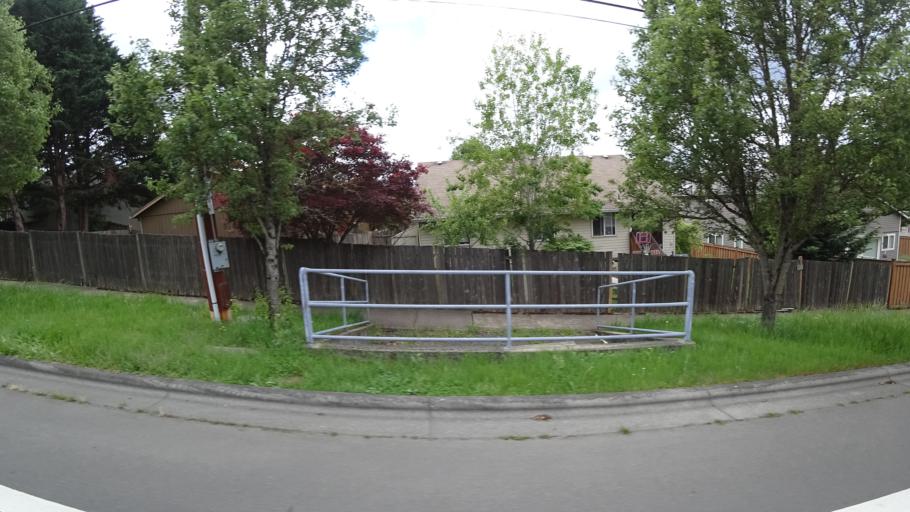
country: US
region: Oregon
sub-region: Washington County
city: Aloha
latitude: 45.4654
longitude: -122.8518
